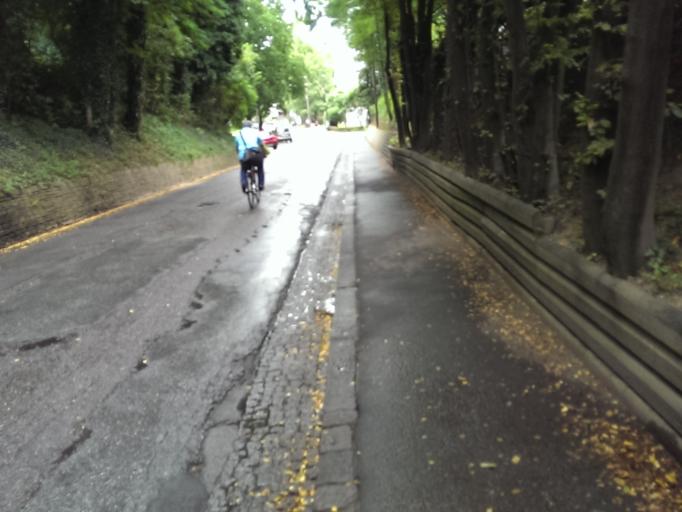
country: AT
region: Styria
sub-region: Graz Stadt
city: Graz
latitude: 47.0659
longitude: 15.4692
